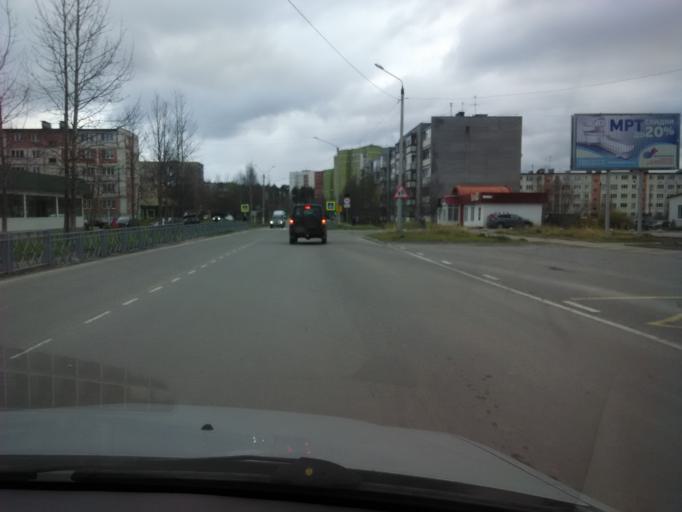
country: RU
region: Murmansk
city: Polyarnyye Zori
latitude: 67.3706
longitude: 32.4868
